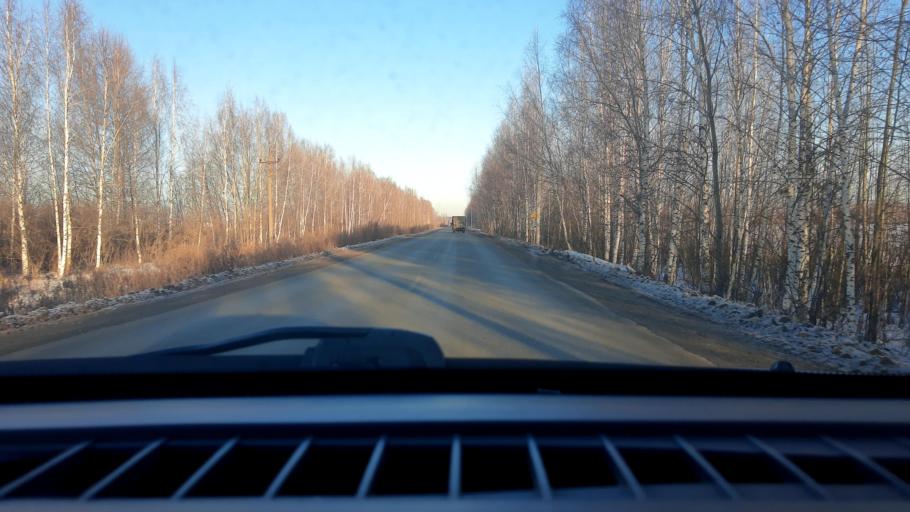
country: RU
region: Nizjnij Novgorod
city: Bor
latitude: 56.3853
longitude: 44.0796
